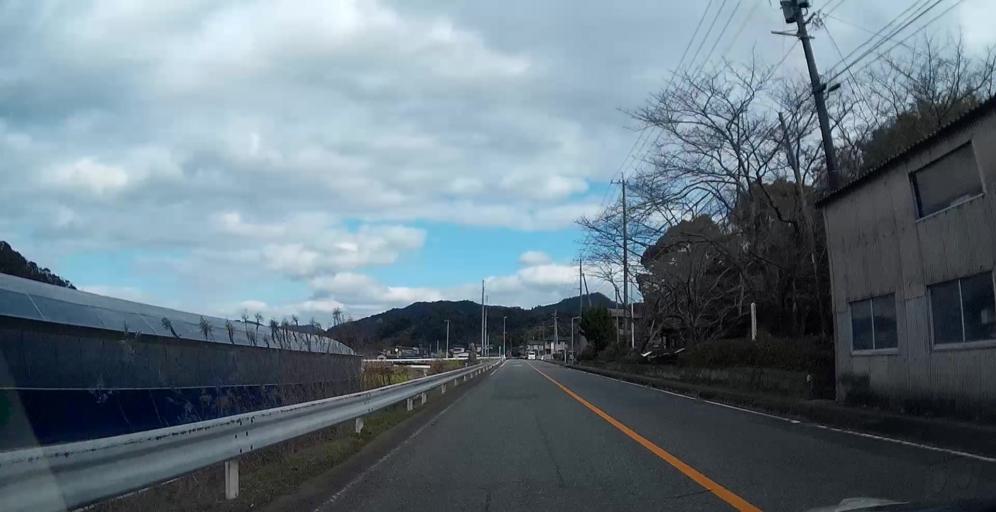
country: JP
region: Kumamoto
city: Minamata
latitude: 32.3431
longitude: 130.5000
